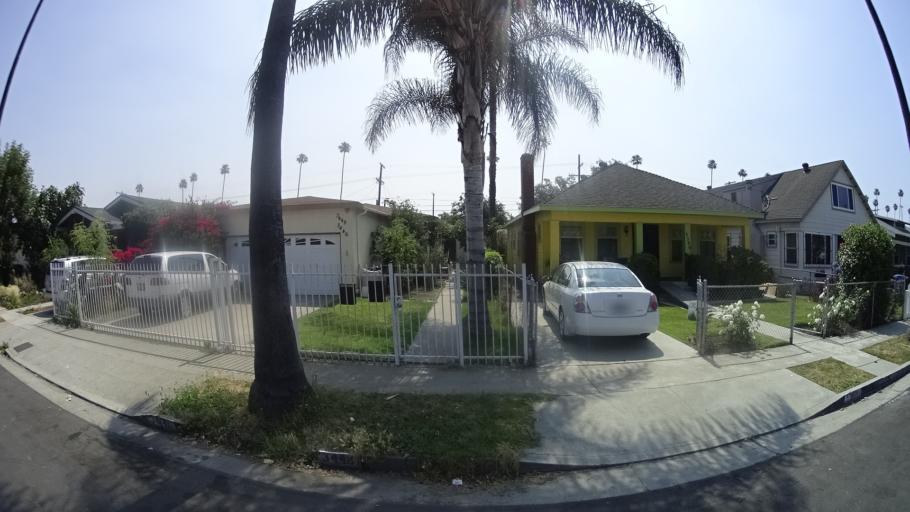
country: US
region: California
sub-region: Los Angeles County
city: View Park-Windsor Hills
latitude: 34.0241
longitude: -118.3260
